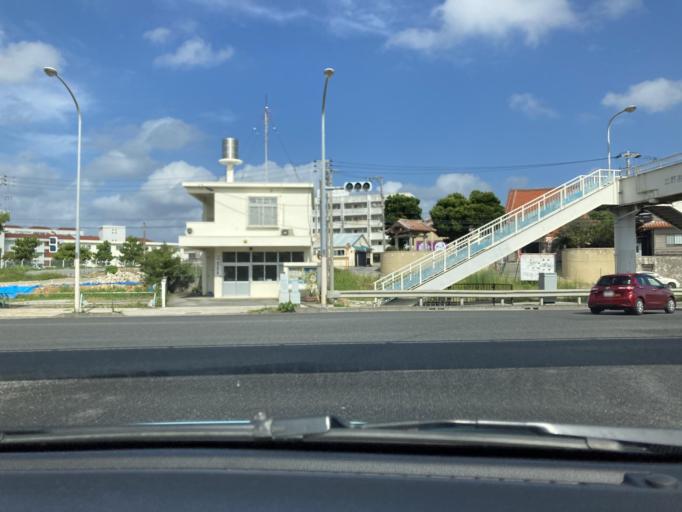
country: JP
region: Okinawa
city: Chatan
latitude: 26.2920
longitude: 127.7772
